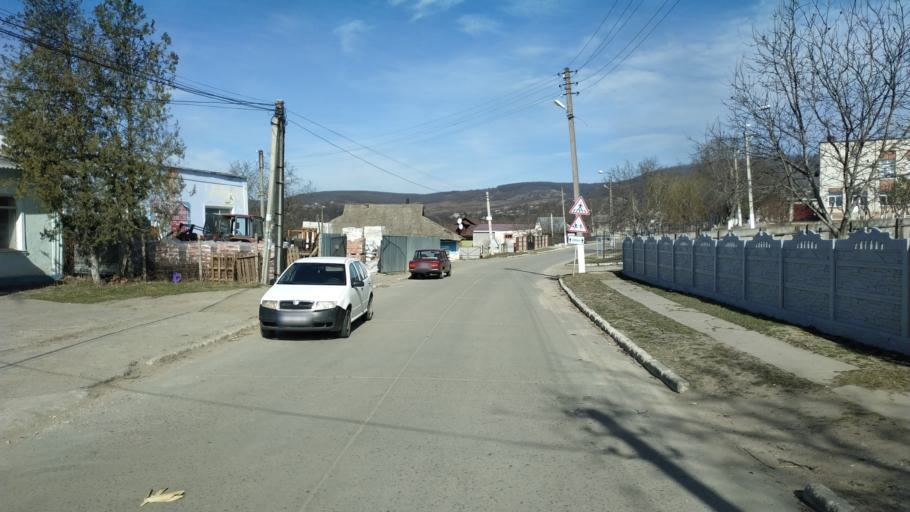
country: MD
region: Nisporeni
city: Nisporeni
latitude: 47.0751
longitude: 28.2606
